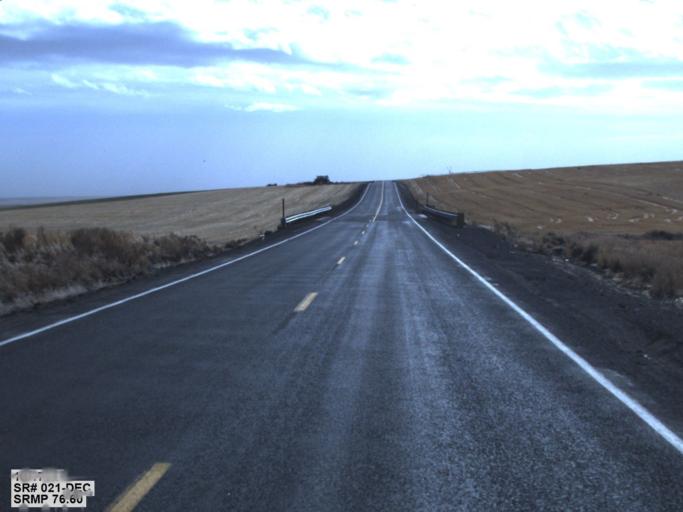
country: US
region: Washington
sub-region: Okanogan County
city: Coulee Dam
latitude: 47.5904
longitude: -118.7861
